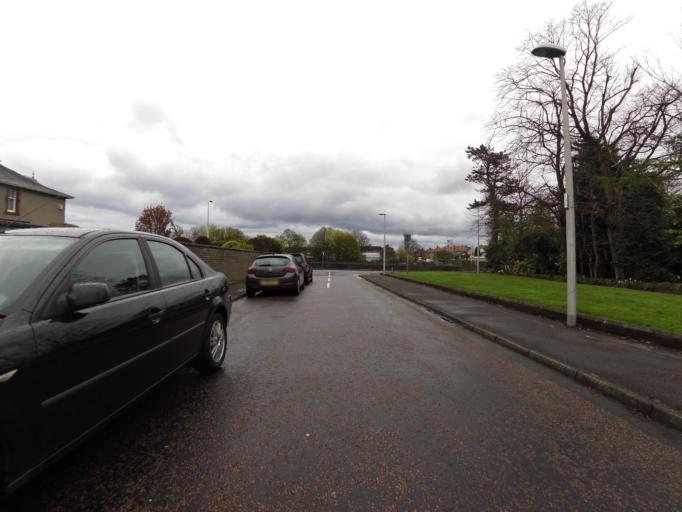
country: GB
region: Scotland
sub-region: Edinburgh
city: Queensferry
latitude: 55.9862
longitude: -3.3975
